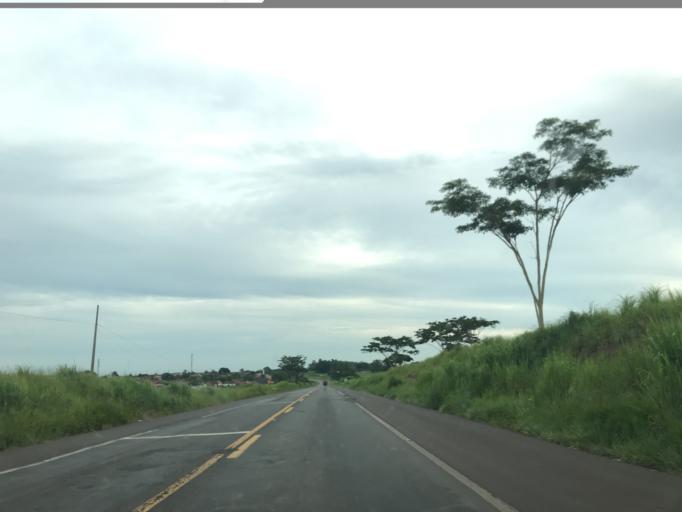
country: BR
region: Sao Paulo
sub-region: Tupa
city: Tupa
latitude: -21.6451
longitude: -50.5070
